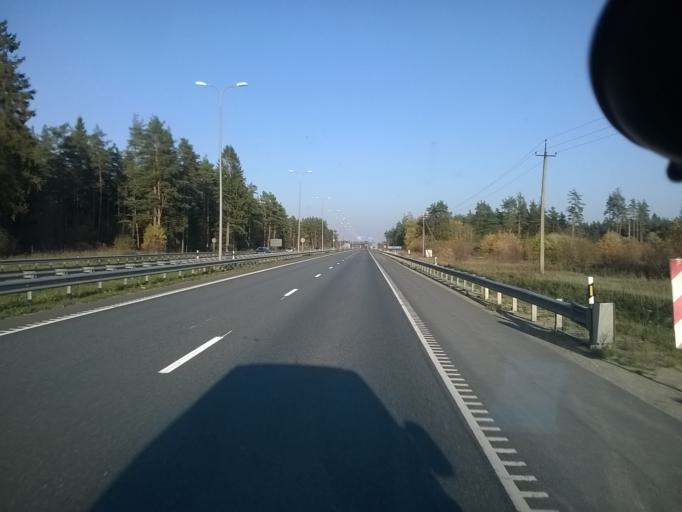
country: EE
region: Harju
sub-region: Kiili vald
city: Kiili
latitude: 59.3163
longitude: 24.7528
